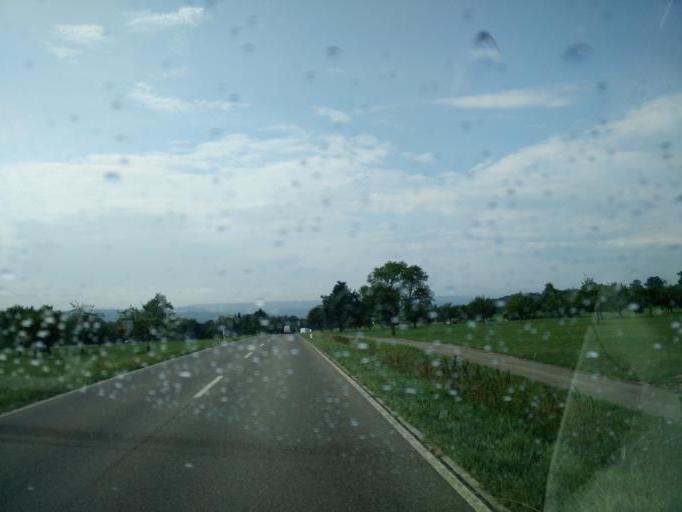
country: DE
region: Baden-Wuerttemberg
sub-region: Tuebingen Region
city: Kusterdingen
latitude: 48.5442
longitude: 9.0931
